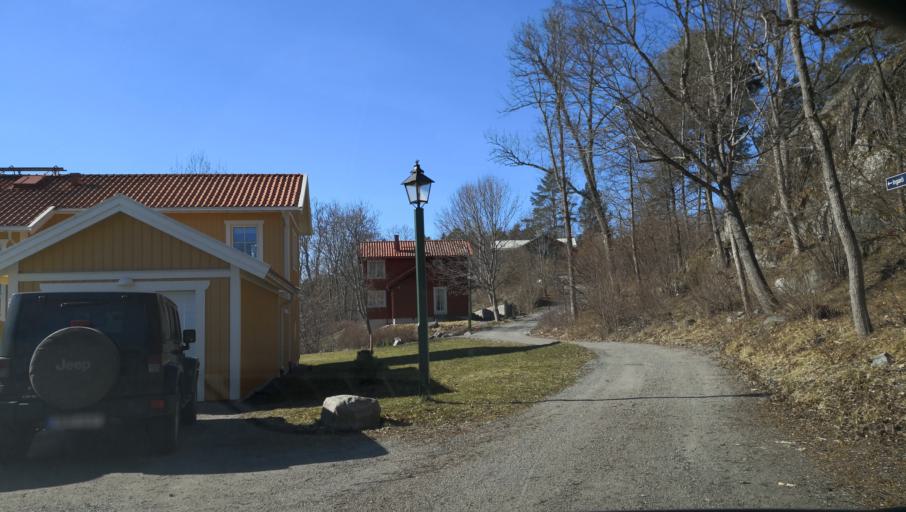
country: SE
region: Stockholm
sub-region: Varmdo Kommun
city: Gustavsberg
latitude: 59.2902
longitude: 18.4052
